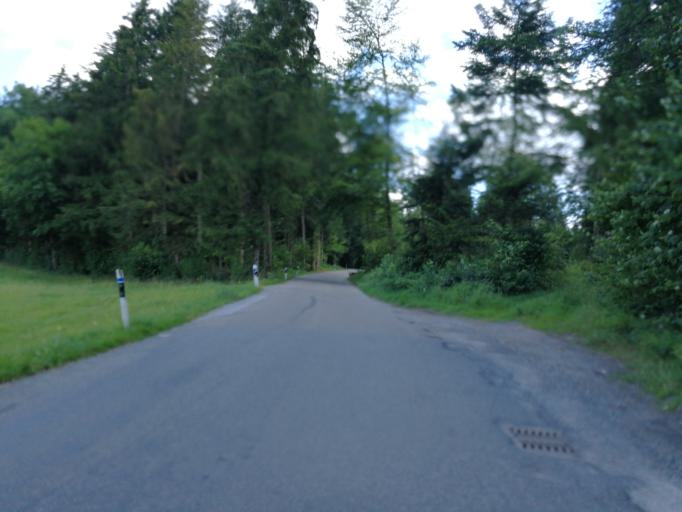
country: CH
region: Zurich
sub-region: Bezirk Hinwil
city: Gossau
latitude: 47.3156
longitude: 8.7640
